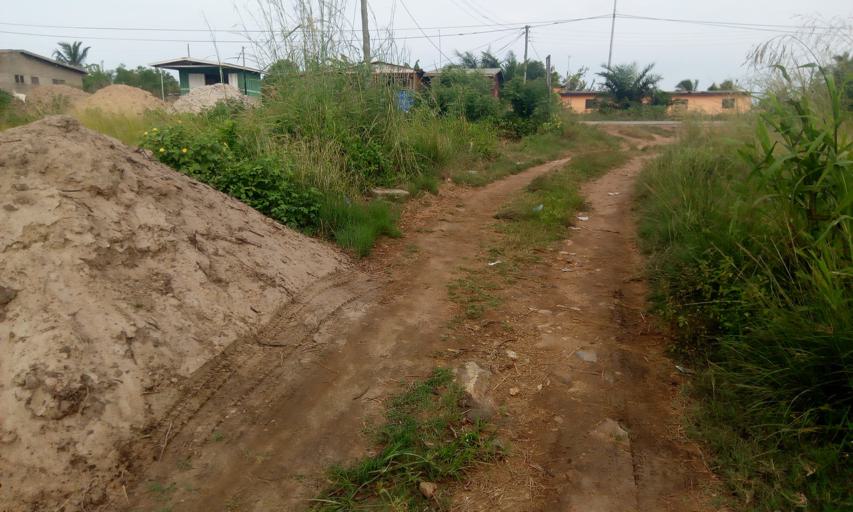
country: GH
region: Central
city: Winneba
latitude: 5.3580
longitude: -0.6242
